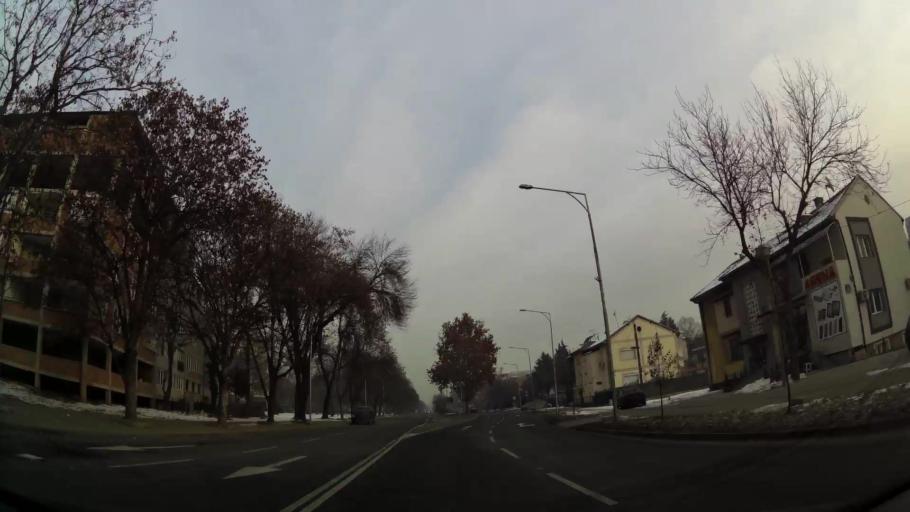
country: MK
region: Cair
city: Cair
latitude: 42.0183
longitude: 21.4478
